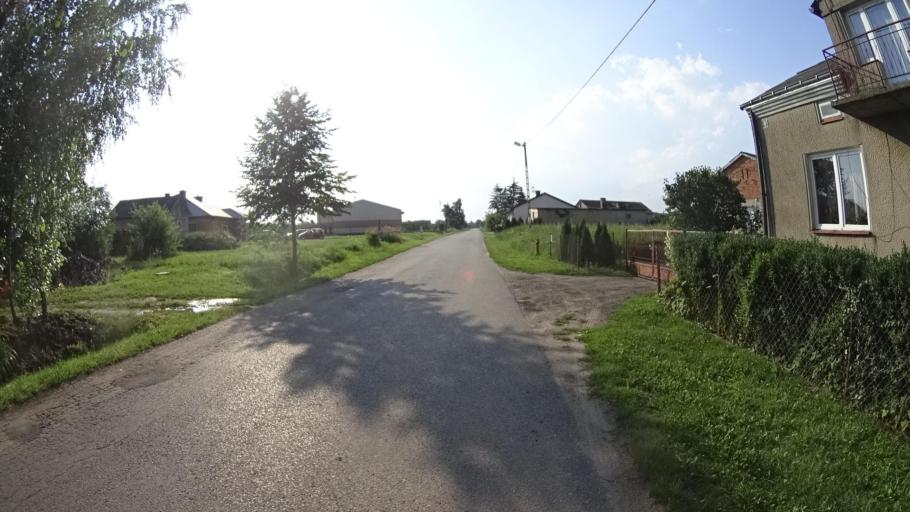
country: PL
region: Masovian Voivodeship
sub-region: Powiat grojecki
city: Goszczyn
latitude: 51.7125
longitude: 20.7887
